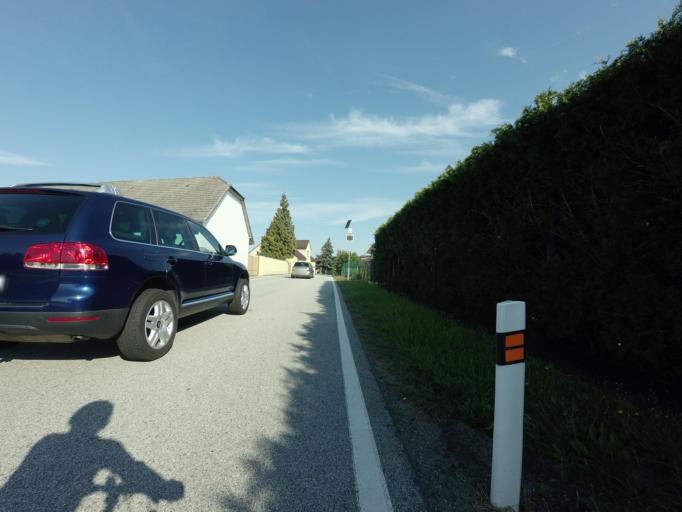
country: CZ
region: Jihocesky
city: Tyn nad Vltavou
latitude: 49.2776
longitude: 14.3994
